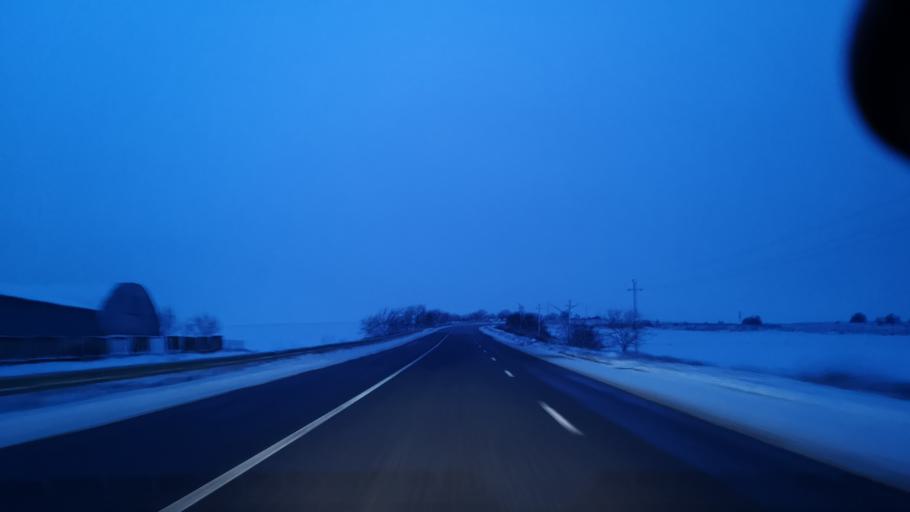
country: MD
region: Rezina
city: Saharna
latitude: 47.5893
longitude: 28.8206
